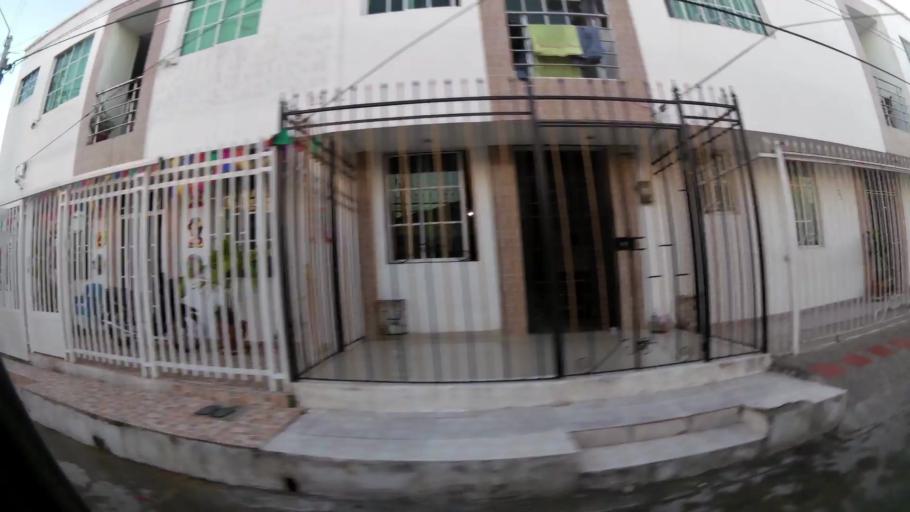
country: CO
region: Atlantico
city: Barranquilla
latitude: 10.9786
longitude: -74.8029
